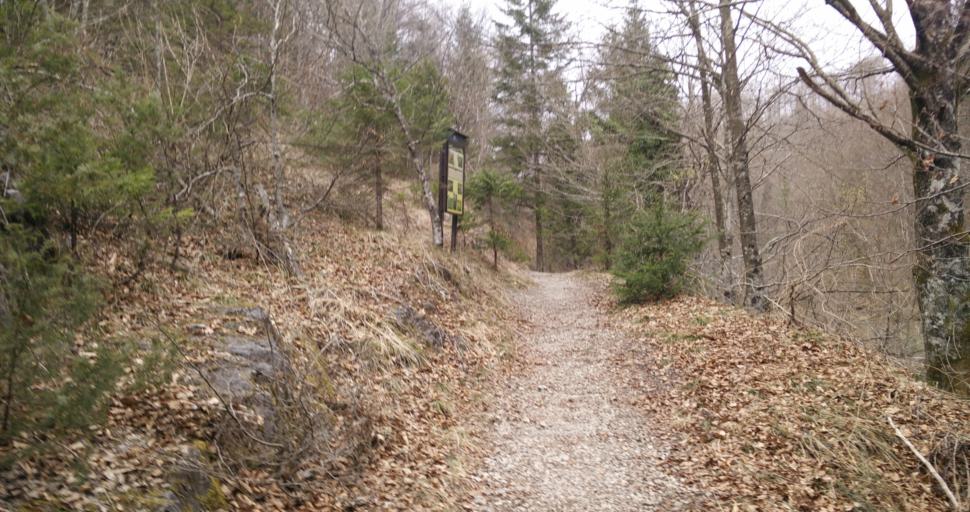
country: HR
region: Primorsko-Goranska
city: Vrbovsko
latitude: 45.3535
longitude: 15.0619
